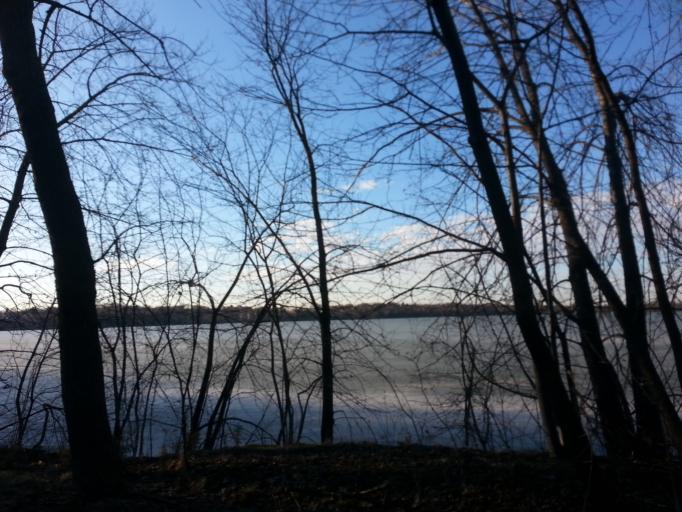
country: US
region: Minnesota
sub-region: Hennepin County
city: Richfield
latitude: 44.9155
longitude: -93.3053
